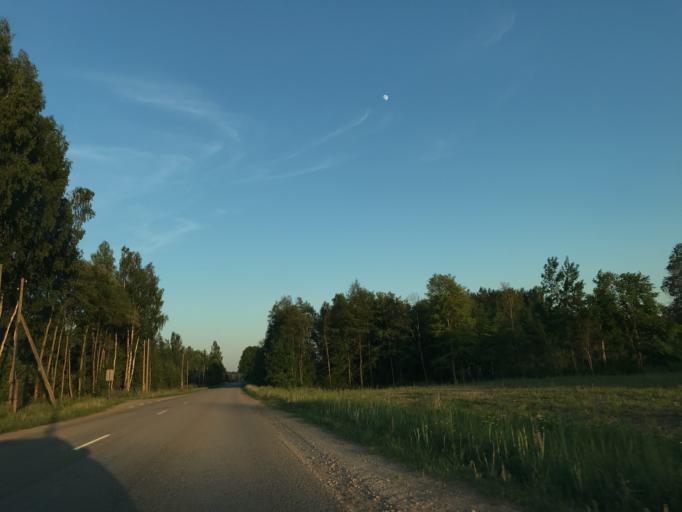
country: LV
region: Jaunjelgava
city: Jaunjelgava
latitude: 56.3601
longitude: 25.0430
